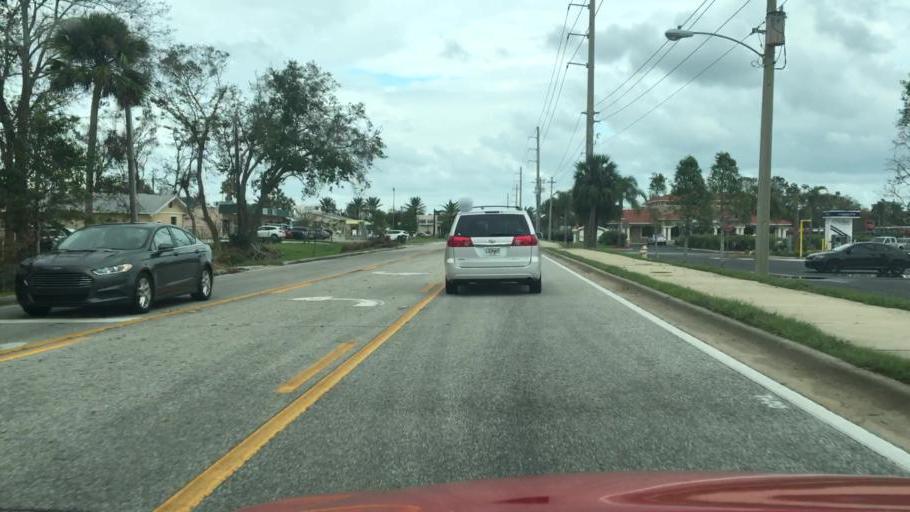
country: US
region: Florida
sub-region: Volusia County
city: South Daytona
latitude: 29.1734
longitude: -81.0055
